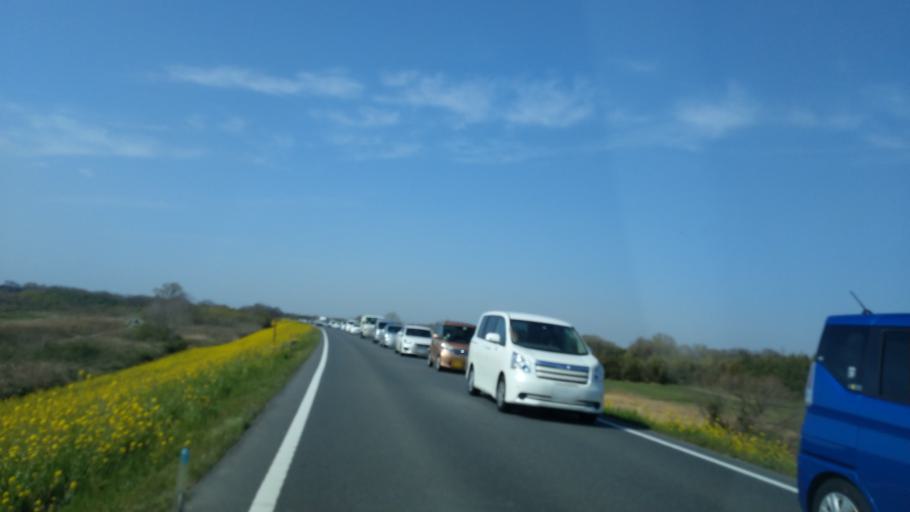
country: JP
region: Saitama
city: Okegawa
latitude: 35.9442
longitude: 139.5360
